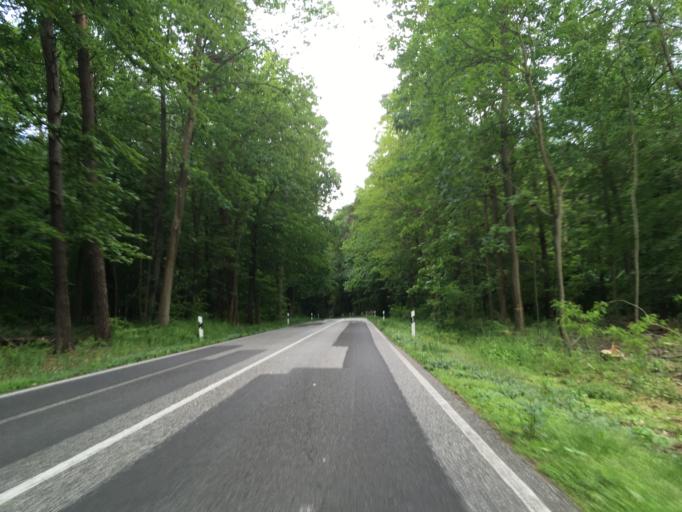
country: DE
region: Brandenburg
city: Bad Freienwalde
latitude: 52.7406
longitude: 13.9903
